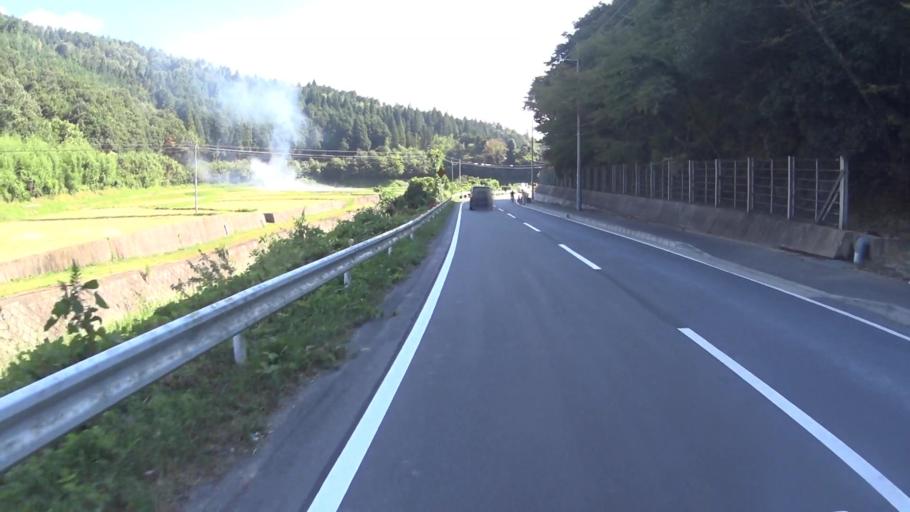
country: JP
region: Kyoto
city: Kameoka
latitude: 34.9520
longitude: 135.5514
